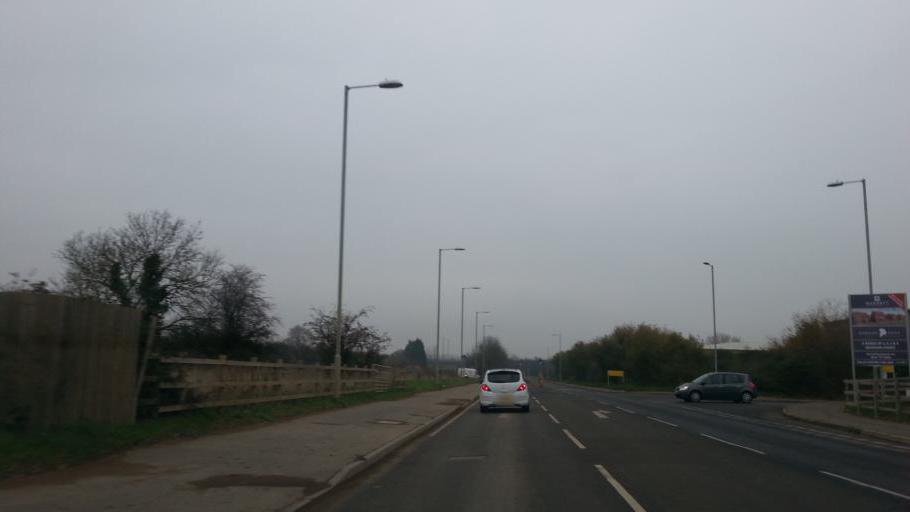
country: GB
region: England
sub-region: Cambridgeshire
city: Godmanchester
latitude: 52.3153
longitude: -0.1619
